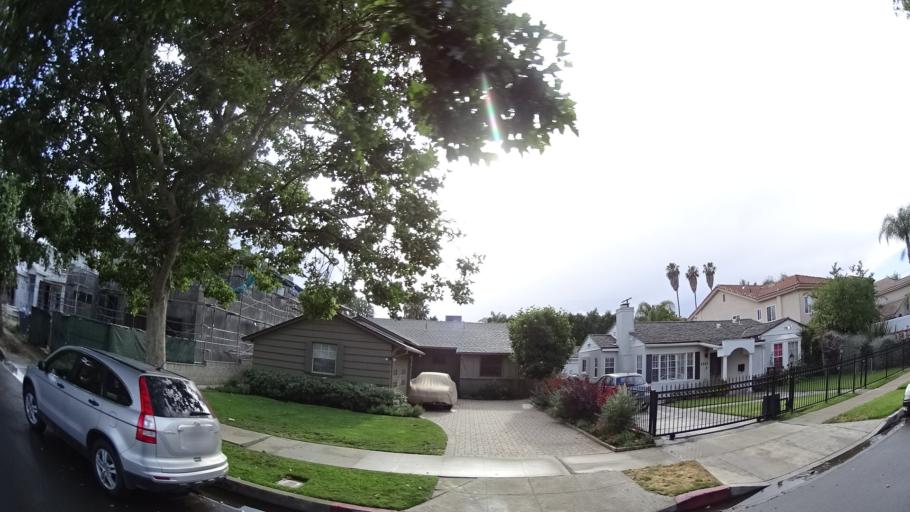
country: US
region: California
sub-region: Los Angeles County
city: Sherman Oaks
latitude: 34.1586
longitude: -118.4465
